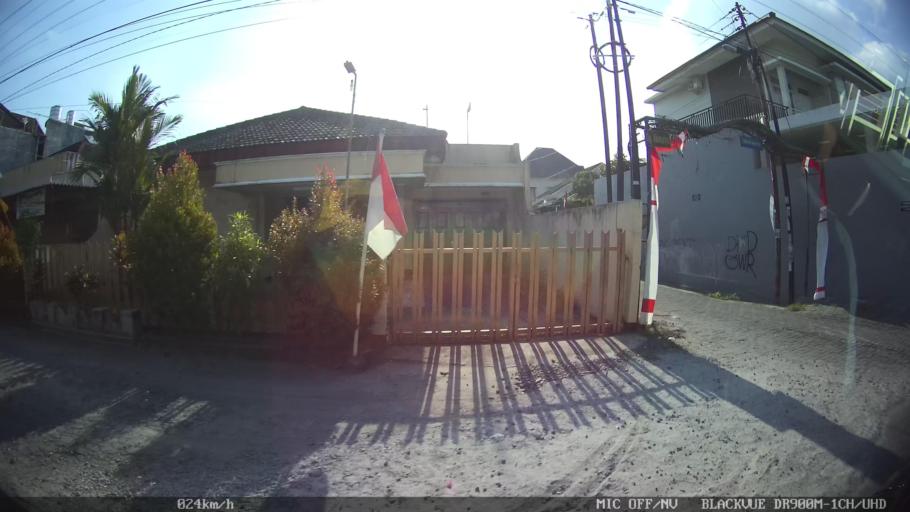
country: ID
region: Daerah Istimewa Yogyakarta
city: Yogyakarta
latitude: -7.8209
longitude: 110.3823
